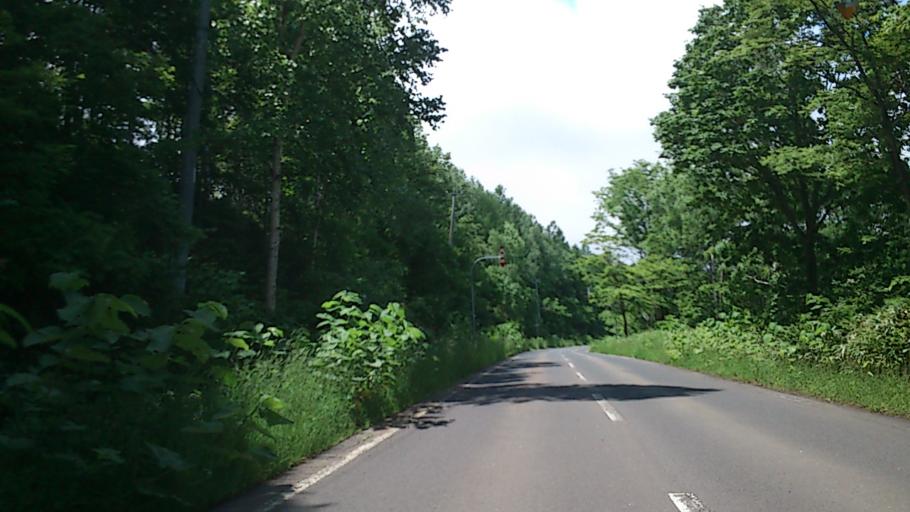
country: JP
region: Hokkaido
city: Niseko Town
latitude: 42.8281
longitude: 140.5357
